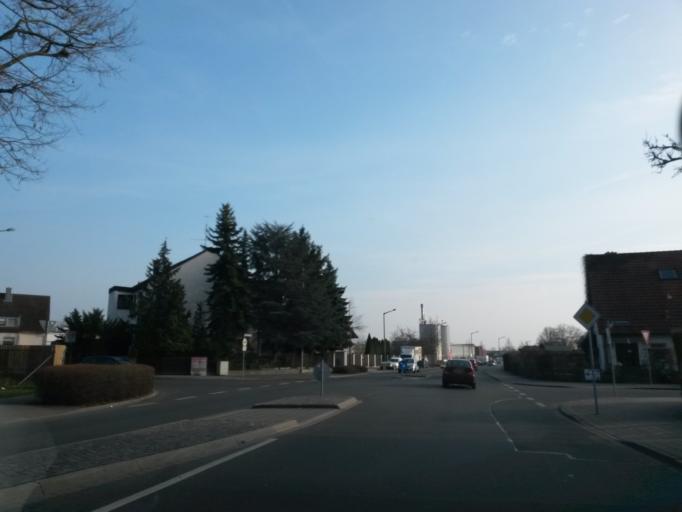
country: DE
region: Bavaria
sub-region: Regierungsbezirk Mittelfranken
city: Furth
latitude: 49.4573
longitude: 11.0042
